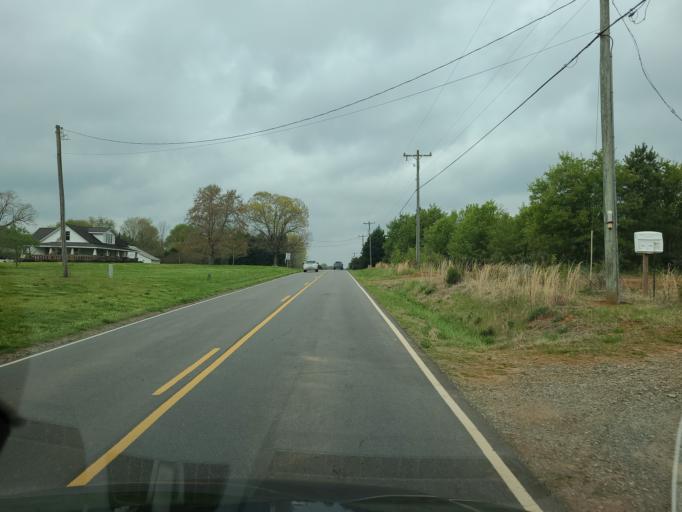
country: US
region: North Carolina
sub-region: Lincoln County
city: Lincolnton
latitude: 35.4570
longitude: -81.3067
